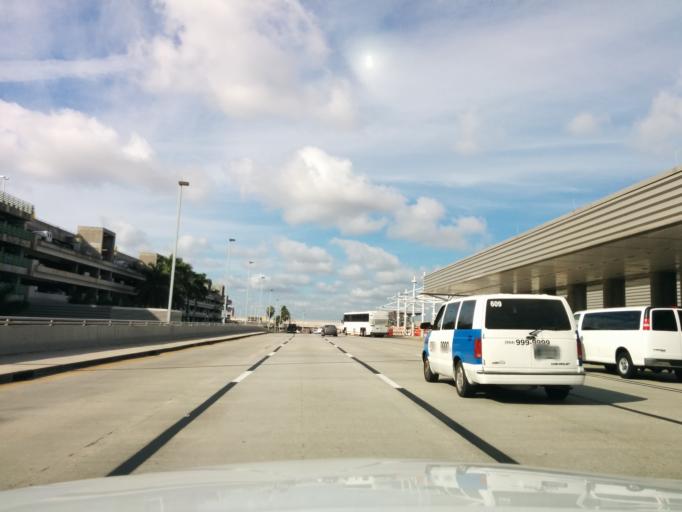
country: US
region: Florida
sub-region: Broward County
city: Dania Beach
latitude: 26.0722
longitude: -80.1400
